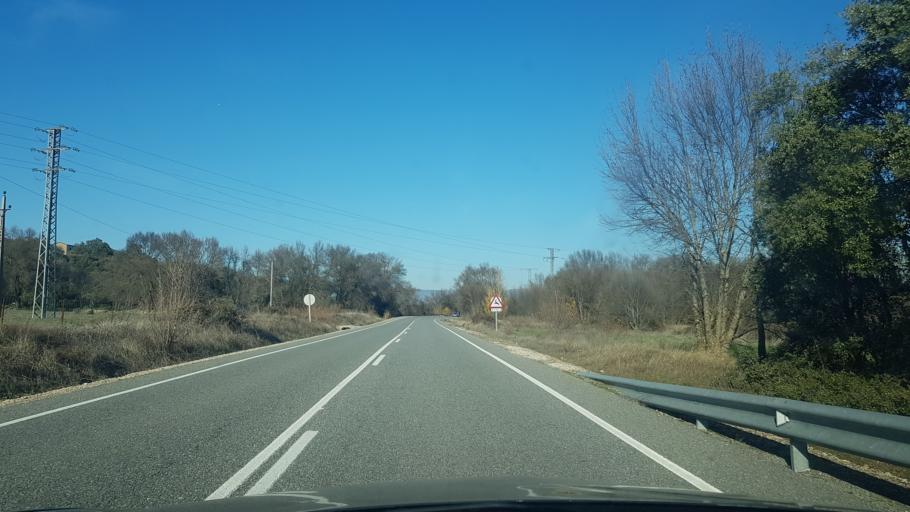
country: ES
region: Madrid
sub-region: Provincia de Madrid
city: San Martin de Valdeiglesias
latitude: 40.3503
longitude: -4.4426
